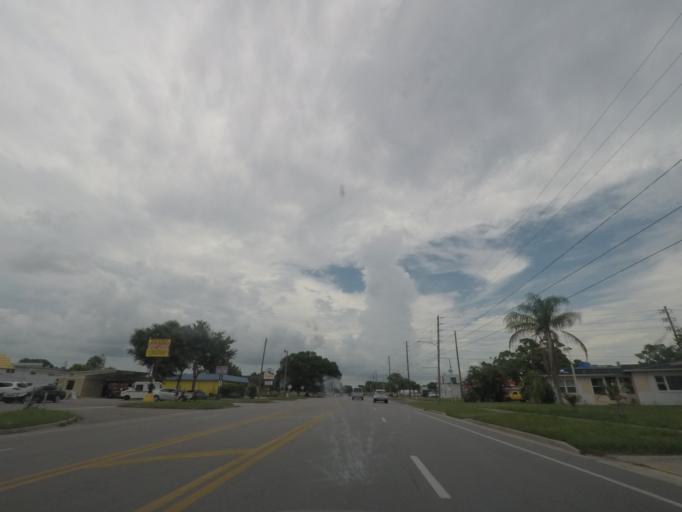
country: US
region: Florida
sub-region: Pinellas County
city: West and East Lealman
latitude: 27.7992
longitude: -82.6822
